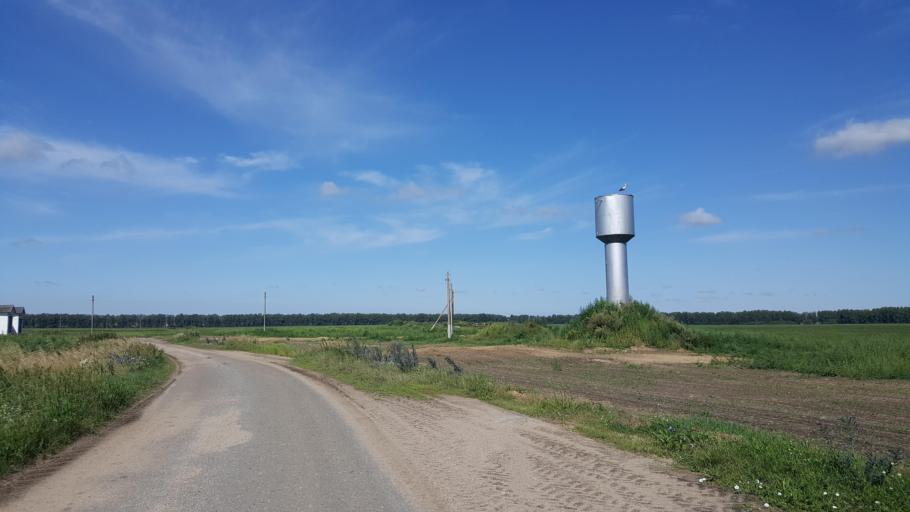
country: BY
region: Brest
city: Charnawchytsy
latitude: 52.3073
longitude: 23.7768
